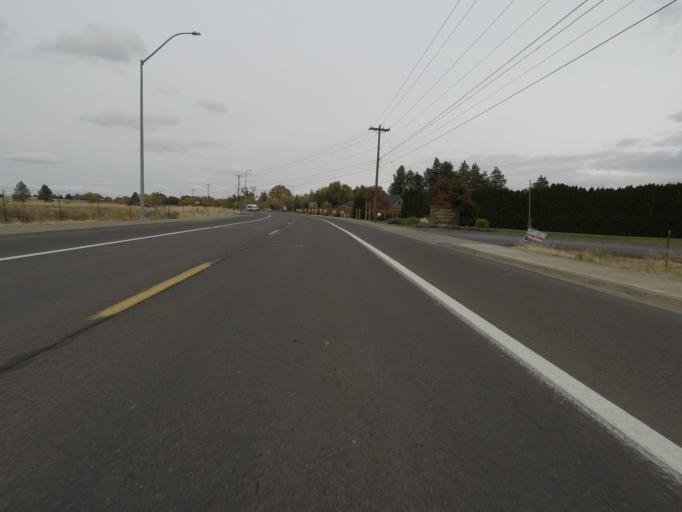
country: US
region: Washington
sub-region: Walla Walla County
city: Walla Walla East
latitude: 46.0741
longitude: -118.2852
